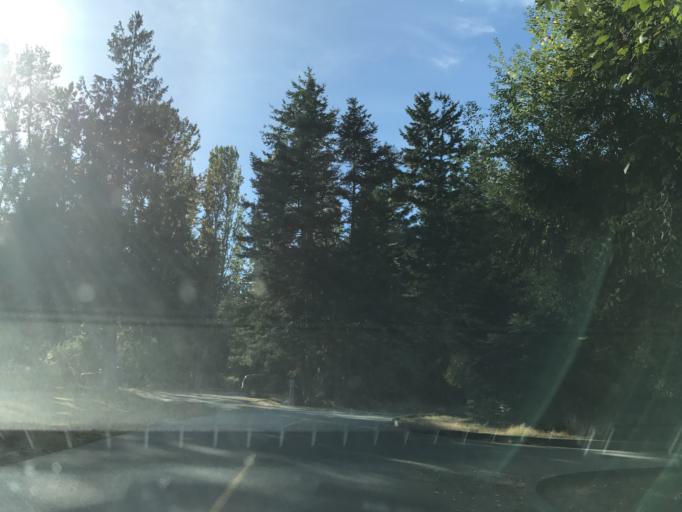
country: US
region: Washington
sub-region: Skagit County
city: Anacortes
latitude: 48.4981
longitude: -122.6922
